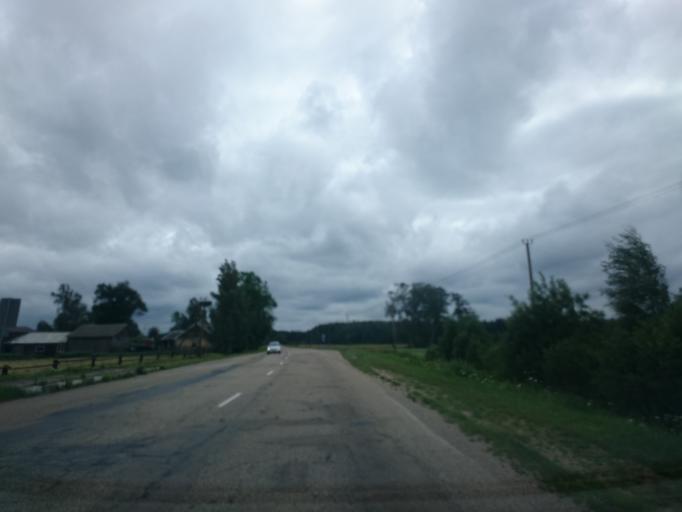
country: LV
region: Pavilostas
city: Pavilosta
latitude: 56.8148
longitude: 21.2264
